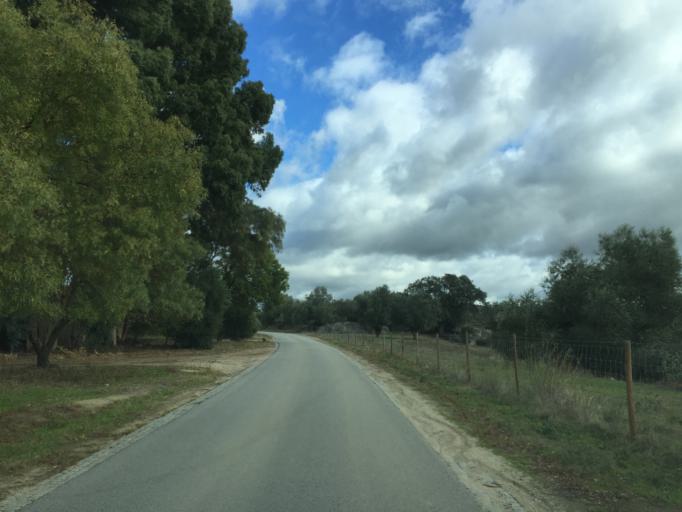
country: PT
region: Portalegre
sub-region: Alter do Chao
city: Alter do Chao
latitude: 39.2208
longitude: -7.6840
